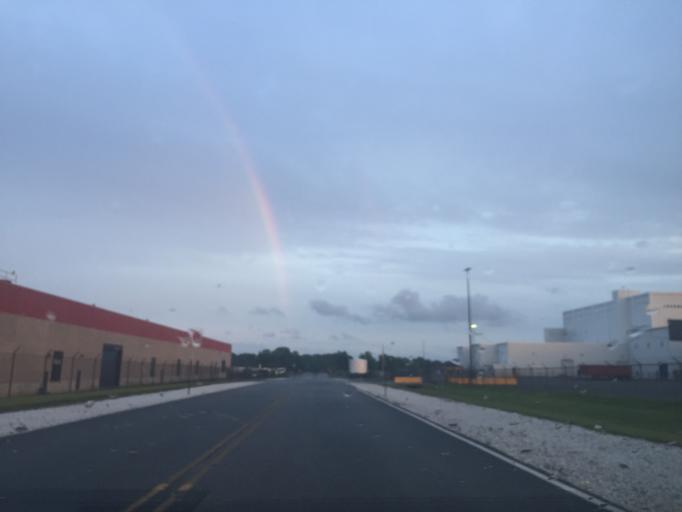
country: US
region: Maryland
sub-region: Baltimore County
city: Middle River
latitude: 39.3317
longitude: -76.4294
